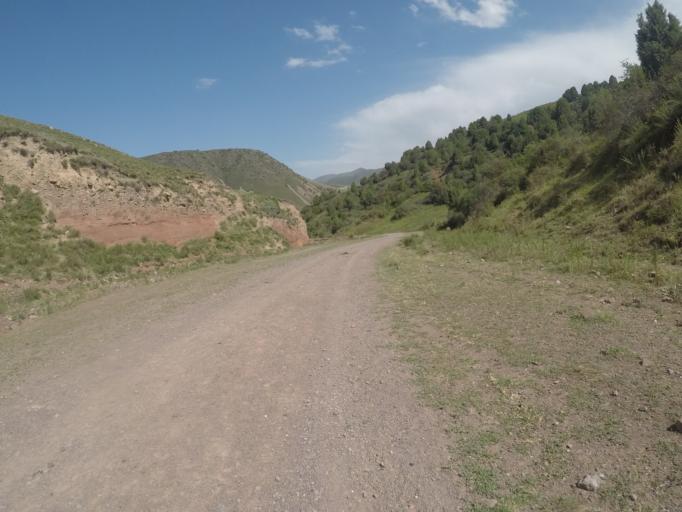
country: KG
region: Chuy
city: Bishkek
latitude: 42.6428
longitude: 74.6073
